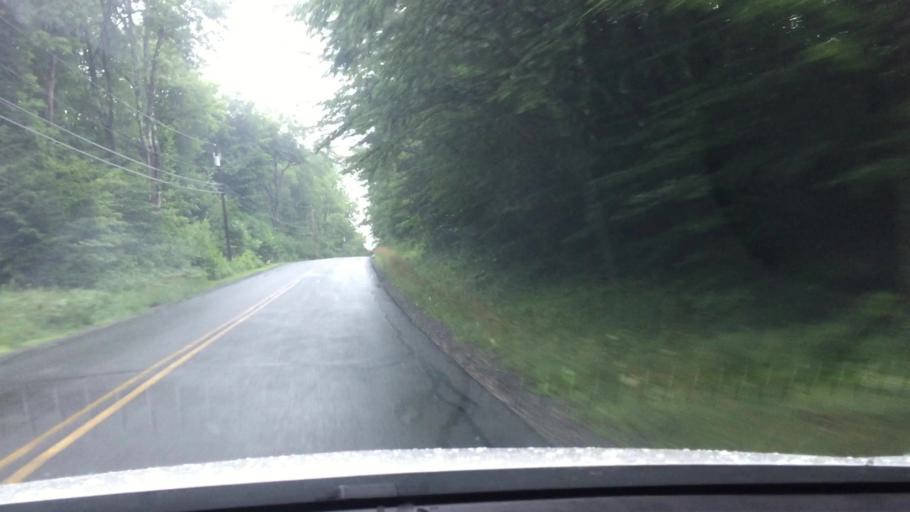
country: US
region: Massachusetts
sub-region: Berkshire County
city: Becket
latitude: 42.2892
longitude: -73.0560
